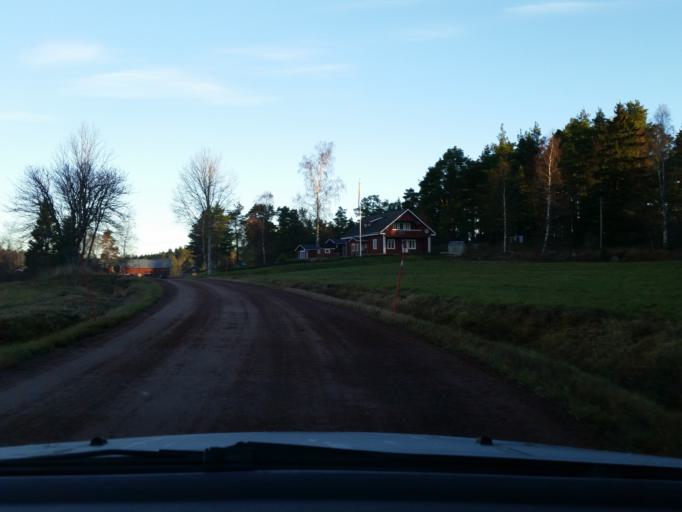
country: AX
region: Alands landsbygd
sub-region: Sund
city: Sund
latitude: 60.2569
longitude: 20.1266
